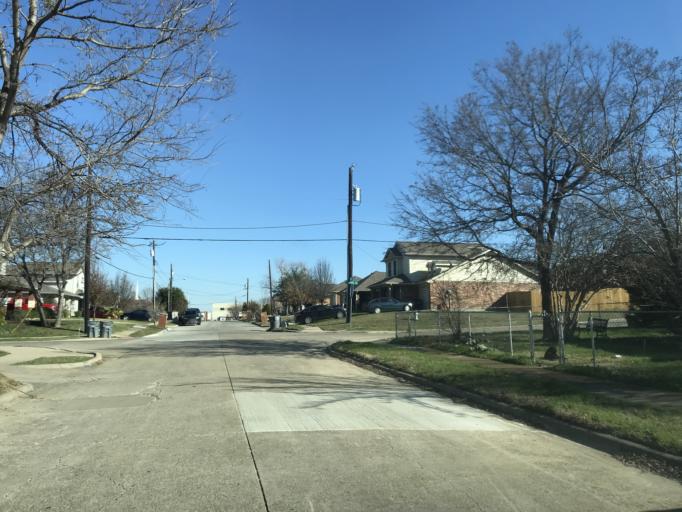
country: US
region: Texas
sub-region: Dallas County
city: Cockrell Hill
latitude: 32.7684
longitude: -96.9057
